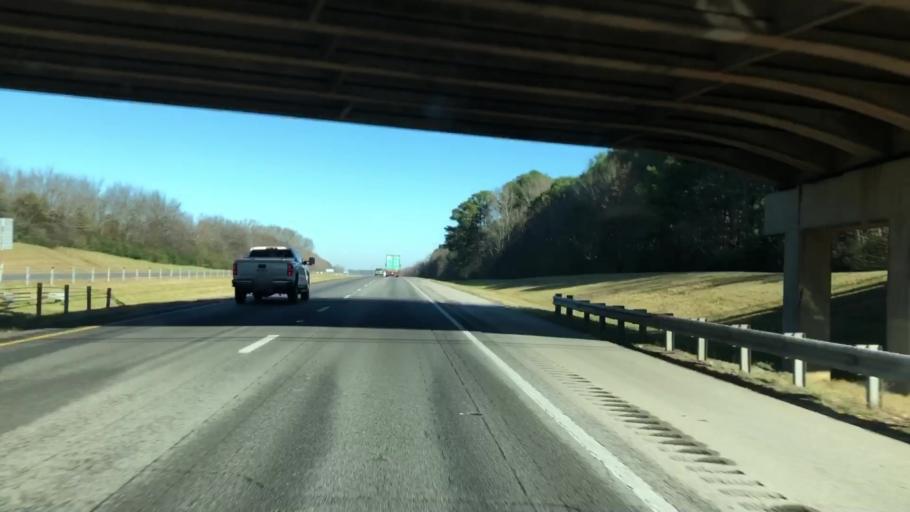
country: US
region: Alabama
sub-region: Limestone County
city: Athens
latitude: 34.7972
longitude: -86.9389
